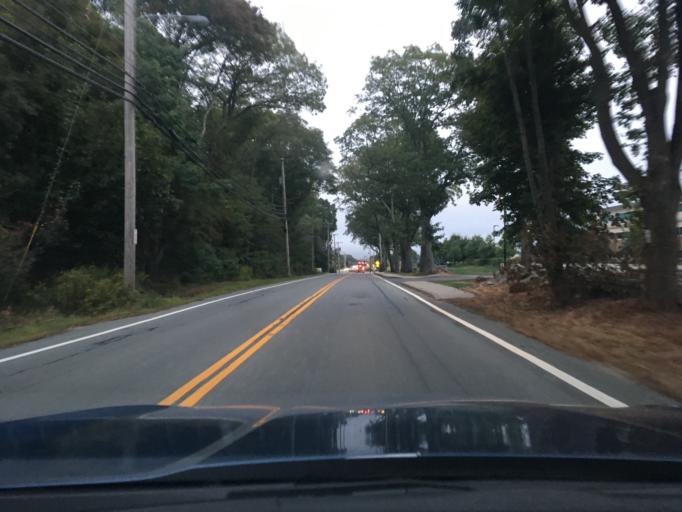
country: US
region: Rhode Island
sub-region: Kent County
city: West Warwick
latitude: 41.6627
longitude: -71.5049
